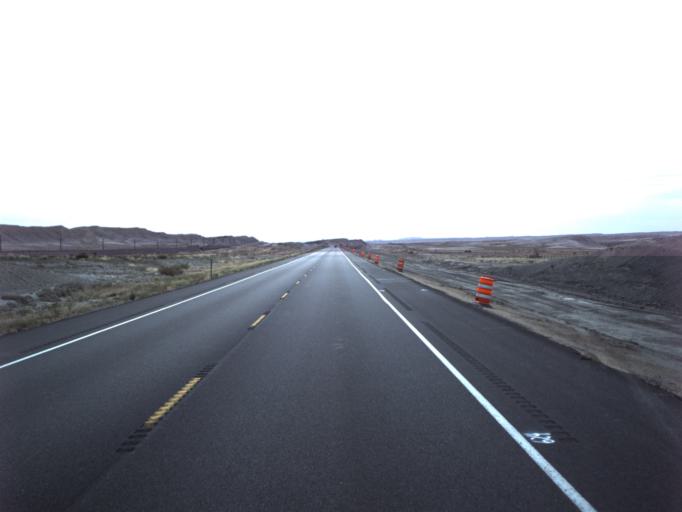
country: US
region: Utah
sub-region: Carbon County
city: East Carbon City
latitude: 39.0496
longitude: -110.3100
